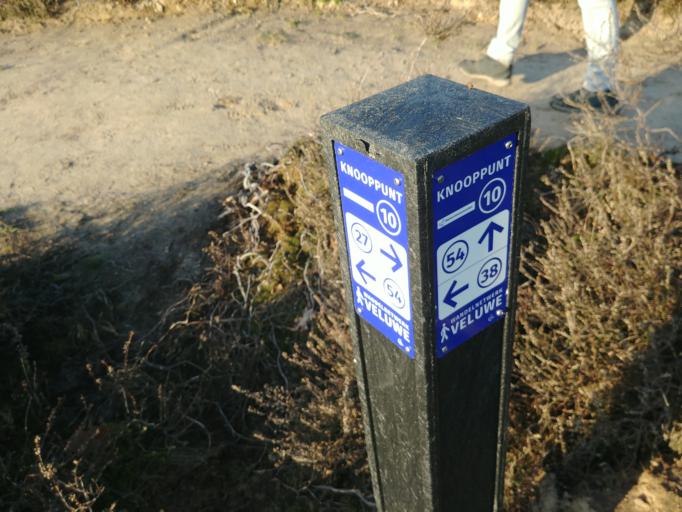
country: NL
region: Gelderland
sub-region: Gemeente Rheden
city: Rheden
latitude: 52.0221
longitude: 6.0268
